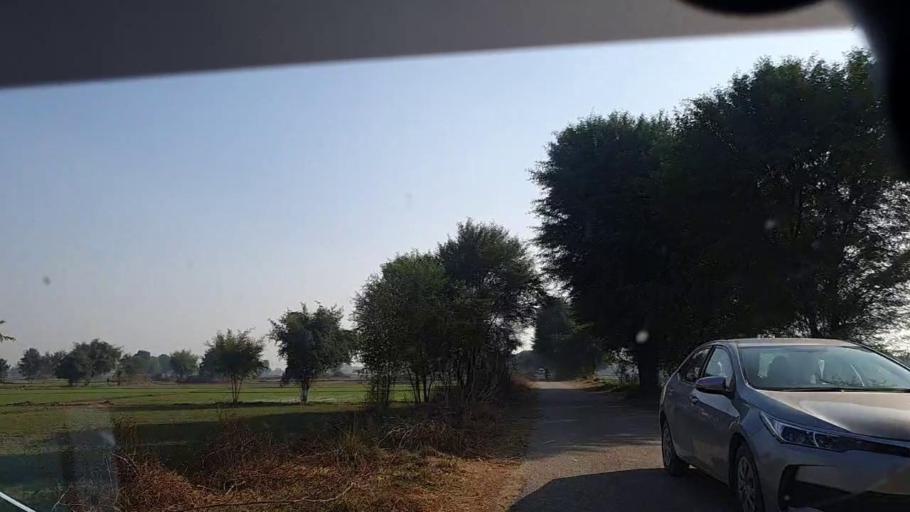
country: PK
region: Sindh
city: Hingorja
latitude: 27.2274
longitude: 68.2690
